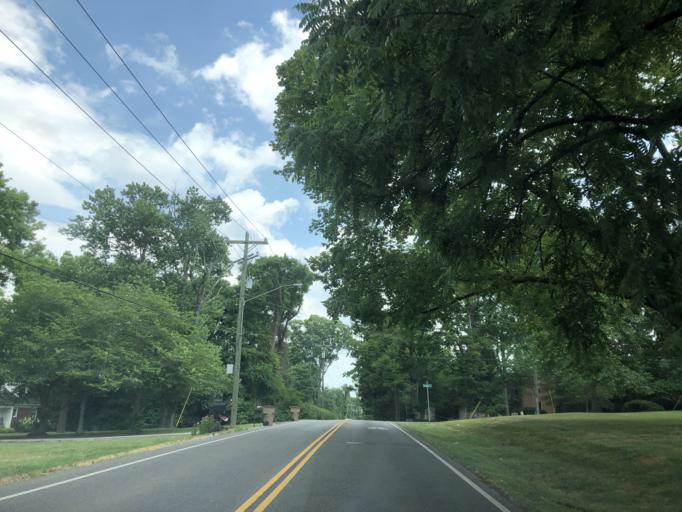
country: US
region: Tennessee
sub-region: Davidson County
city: Belle Meade
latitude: 36.1236
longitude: -86.8235
